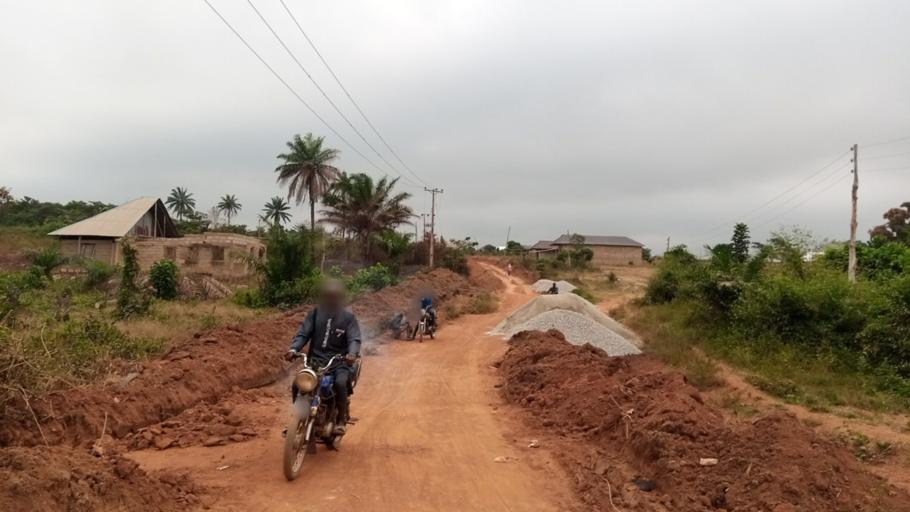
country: NG
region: Osun
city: Osogbo
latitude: 7.7627
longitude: 4.6233
